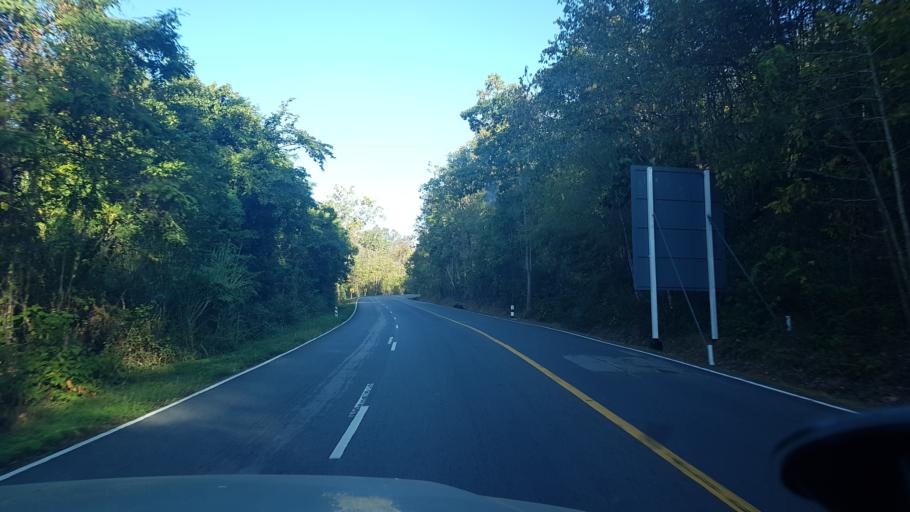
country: TH
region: Phetchabun
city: Nam Nao
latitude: 16.6981
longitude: 101.6637
